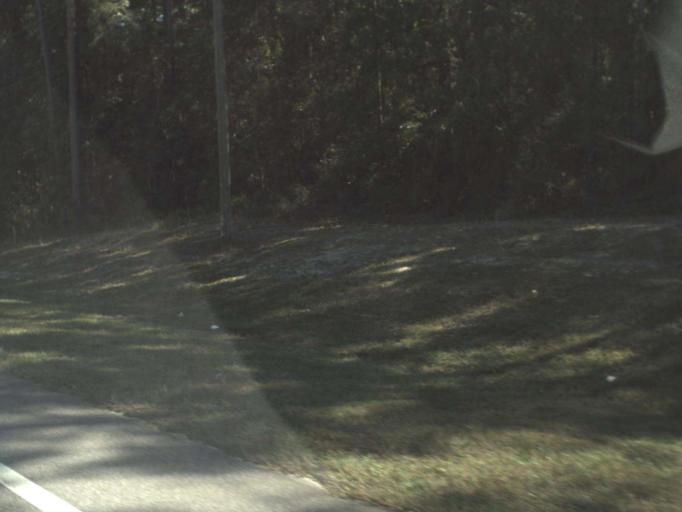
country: US
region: Florida
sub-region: Walton County
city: Freeport
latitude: 30.4876
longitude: -86.1137
